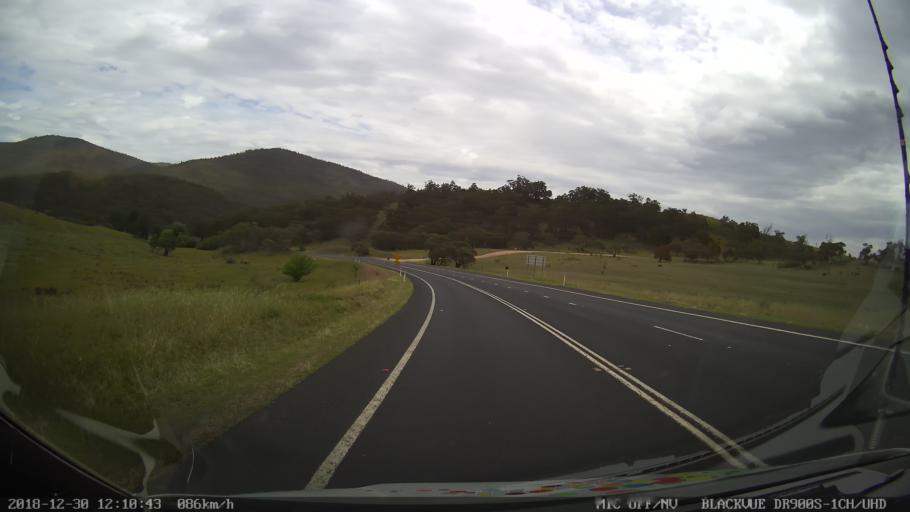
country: AU
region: New South Wales
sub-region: Snowy River
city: Jindabyne
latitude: -36.3716
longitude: 148.5954
